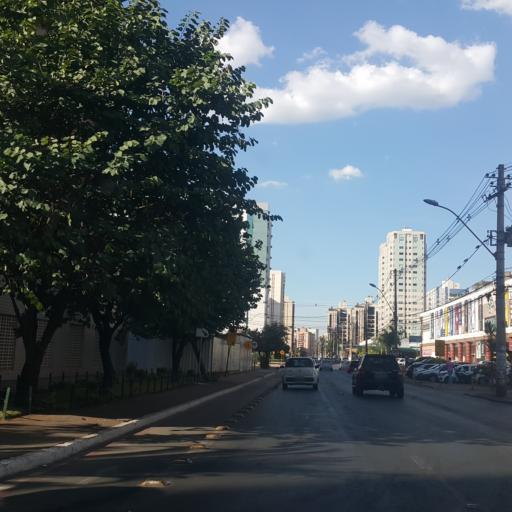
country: BR
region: Federal District
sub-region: Brasilia
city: Brasilia
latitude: -15.8405
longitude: -48.0220
